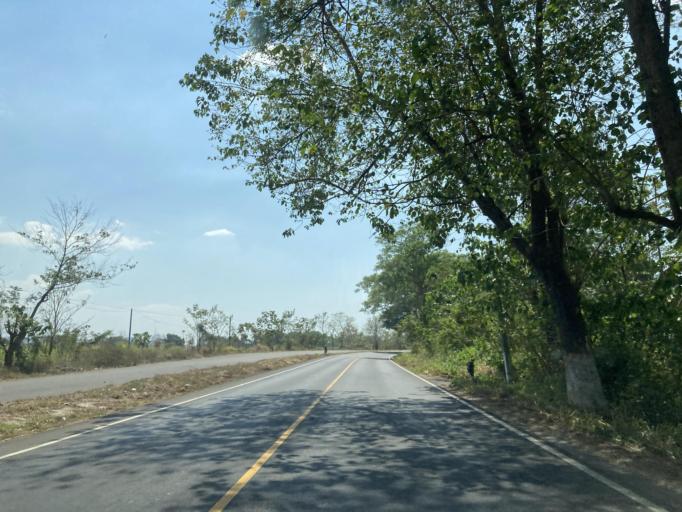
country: GT
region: Escuintla
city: Guanagazapa
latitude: 14.1945
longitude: -90.6969
